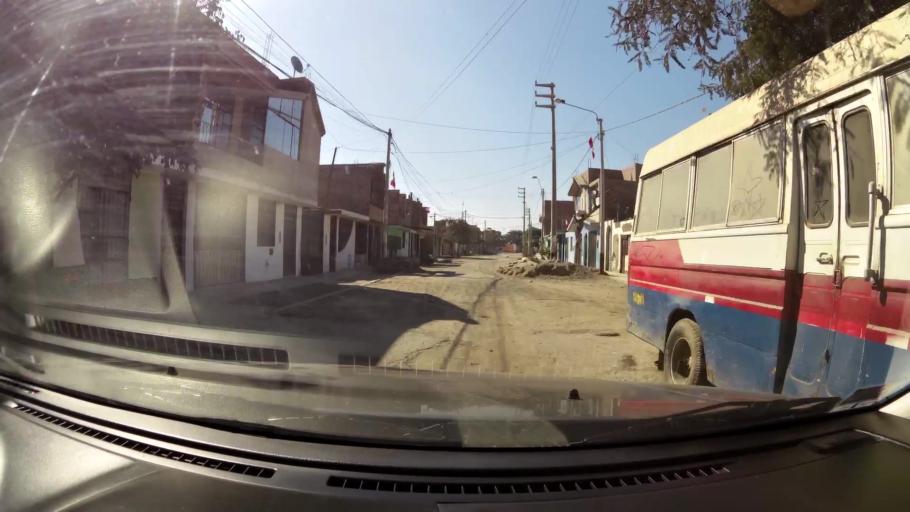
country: PE
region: Ica
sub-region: Provincia de Ica
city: La Tinguina
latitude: -14.0344
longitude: -75.7118
